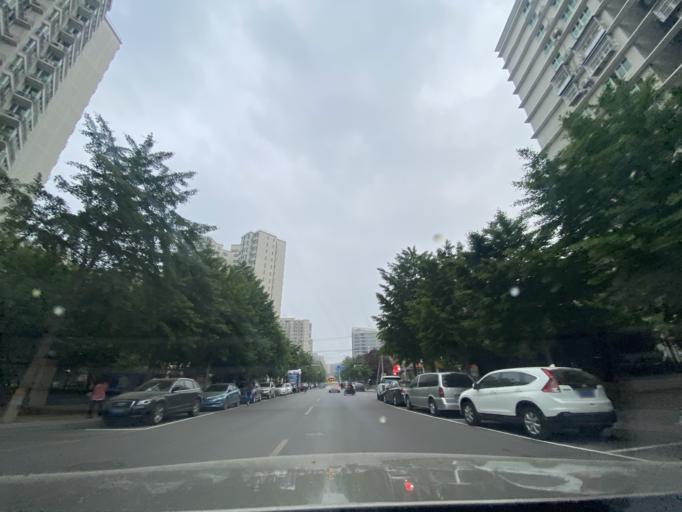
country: CN
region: Beijing
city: Sijiqing
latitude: 39.9596
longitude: 116.2743
